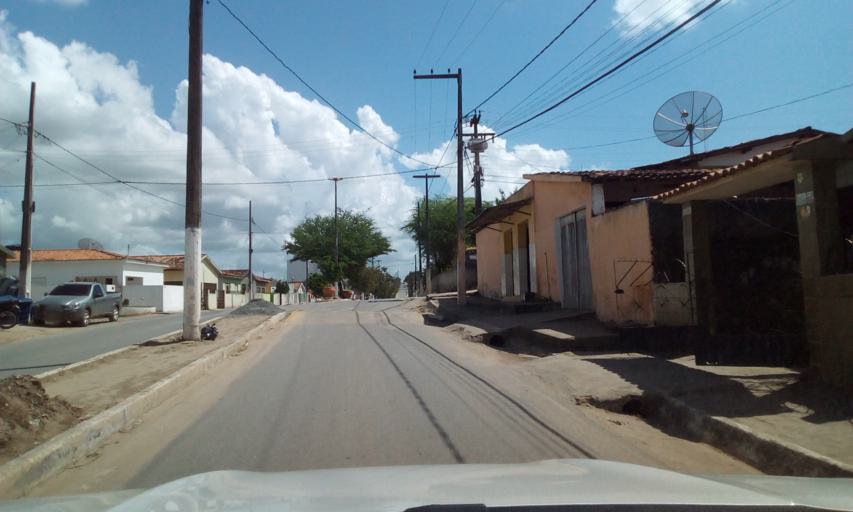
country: BR
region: Paraiba
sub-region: Guarabira
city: Guarabira
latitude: -6.8515
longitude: -35.3826
